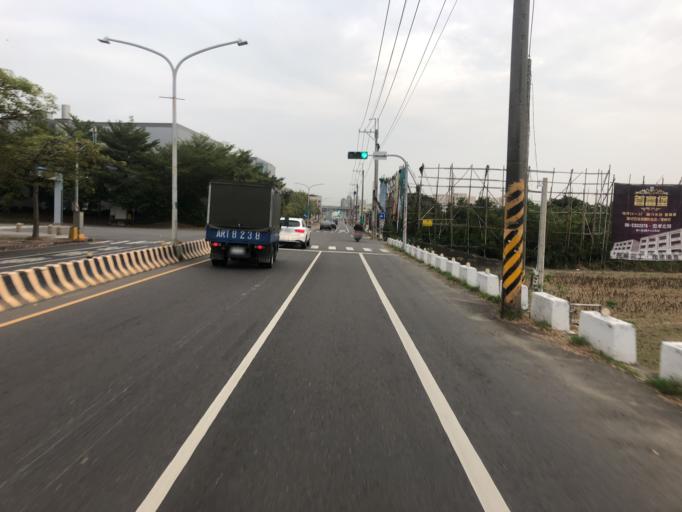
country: TW
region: Taiwan
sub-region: Tainan
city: Tainan
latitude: 23.0831
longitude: 120.2826
